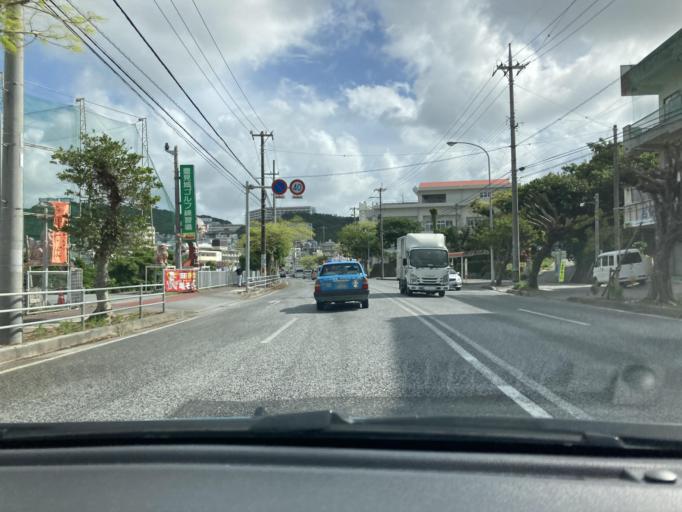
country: JP
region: Okinawa
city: Tomigusuku
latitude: 26.1789
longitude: 127.6812
